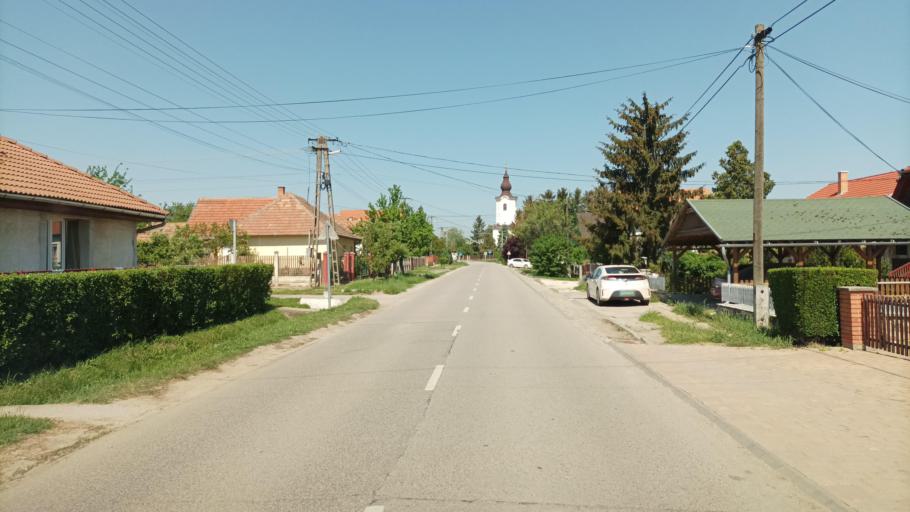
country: HU
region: Pest
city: Uri
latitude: 47.4111
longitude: 19.5248
